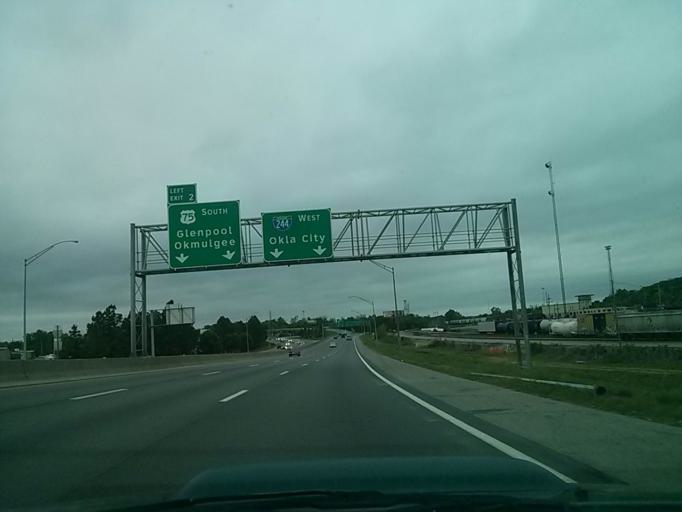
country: US
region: Oklahoma
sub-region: Tulsa County
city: Tulsa
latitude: 36.1178
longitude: -96.0094
